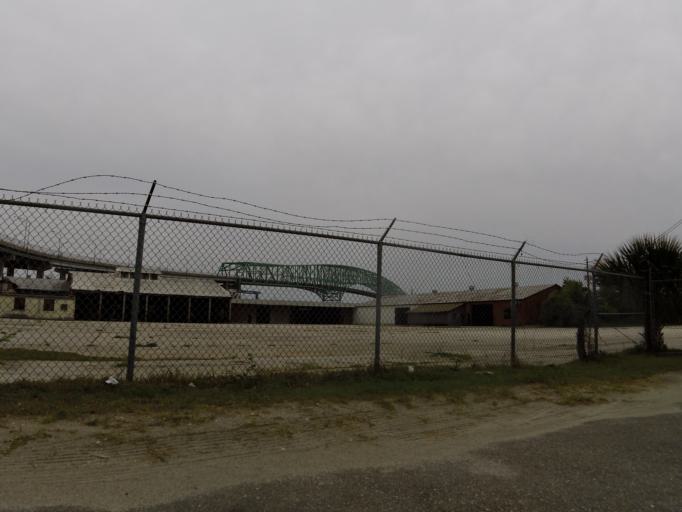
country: US
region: Florida
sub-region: Duval County
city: Jacksonville
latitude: 30.3200
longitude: -81.6330
